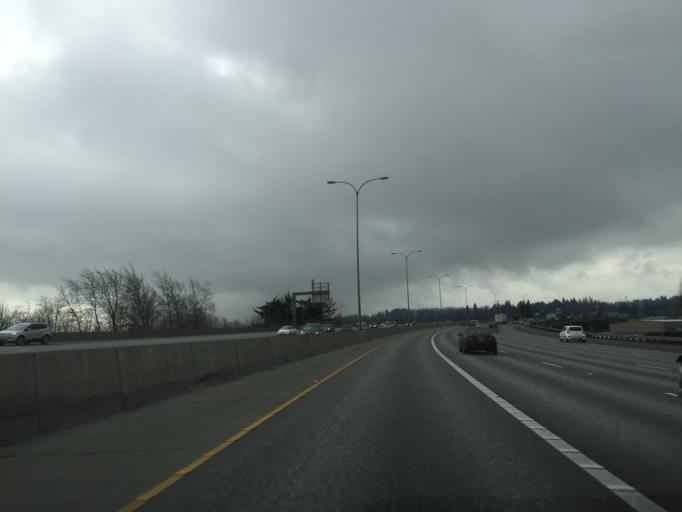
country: US
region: Washington
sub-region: Snohomish County
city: Everett
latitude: 47.9738
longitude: -122.1914
